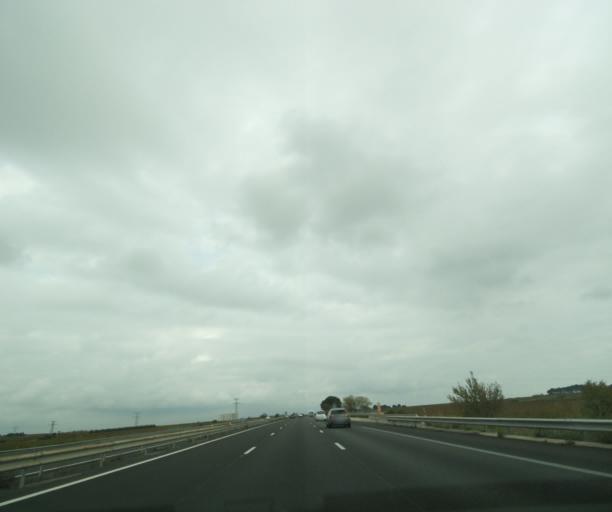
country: FR
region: Languedoc-Roussillon
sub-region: Departement de l'Herault
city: Florensac
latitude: 43.4017
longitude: 3.4775
